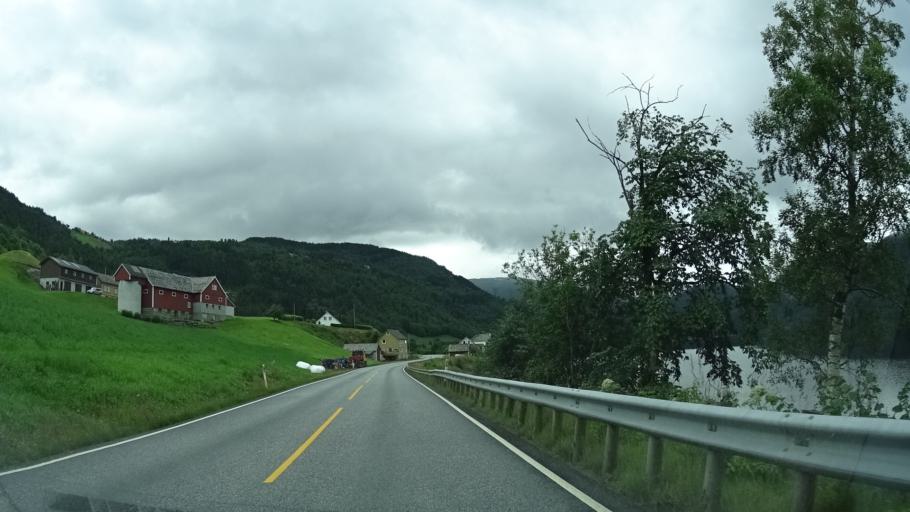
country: NO
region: Hordaland
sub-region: Granvin
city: Granvin
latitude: 60.5615
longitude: 6.7270
